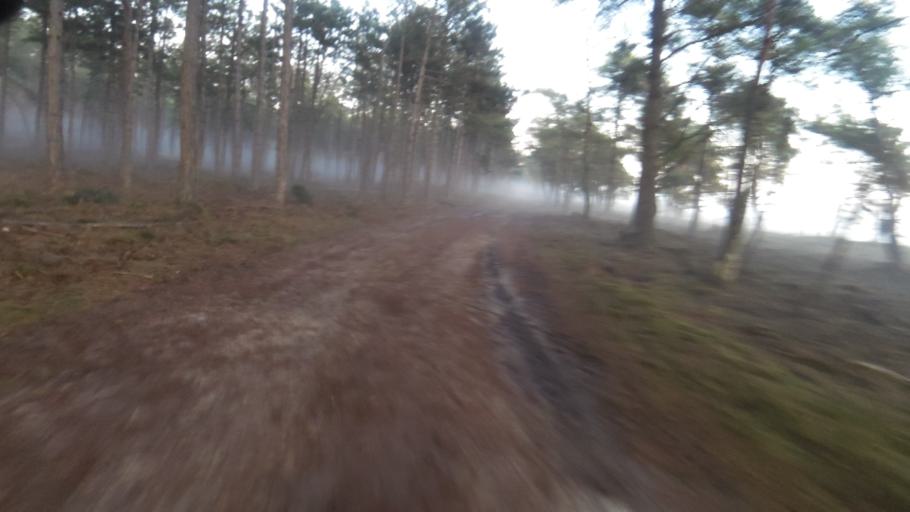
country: NL
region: Gelderland
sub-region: Gemeente Apeldoorn
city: Uddel
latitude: 52.2482
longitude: 5.7861
